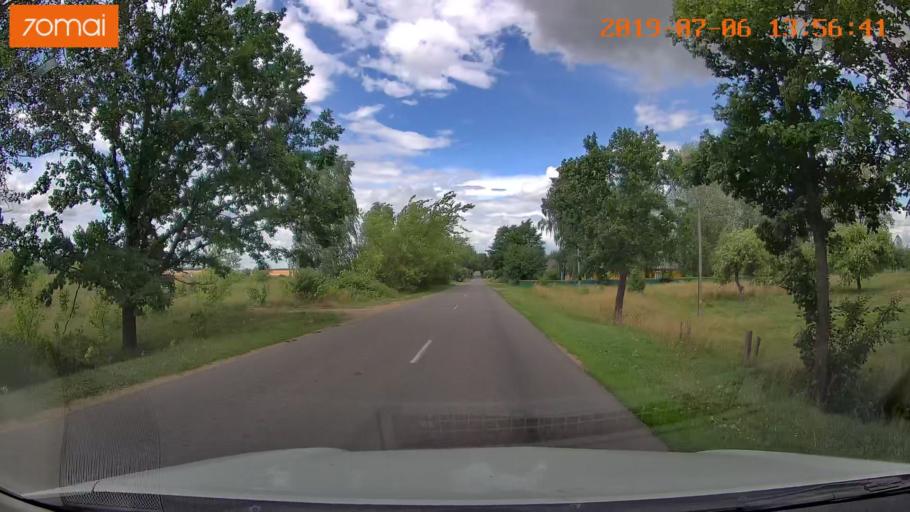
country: BY
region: Minsk
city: Ivyanyets
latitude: 53.7674
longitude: 26.8046
